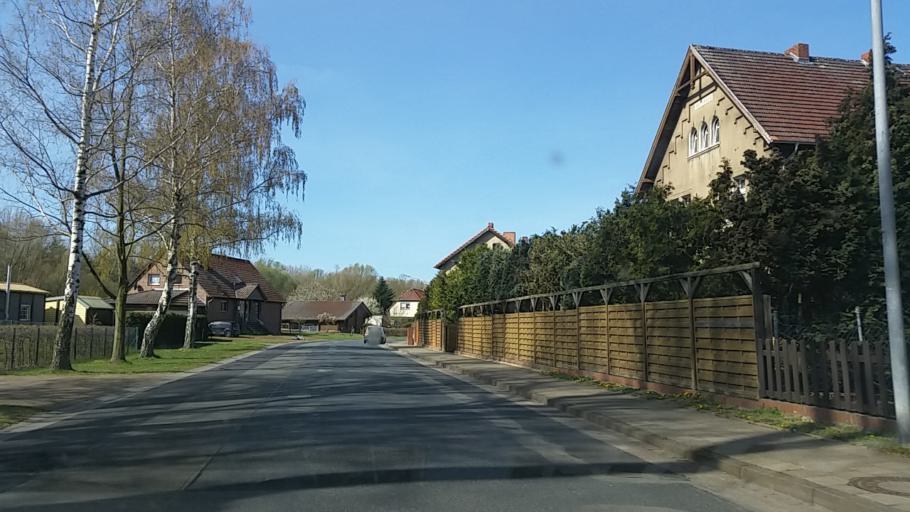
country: DE
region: Lower Saxony
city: Jerxheim
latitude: 52.0672
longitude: 10.8813
